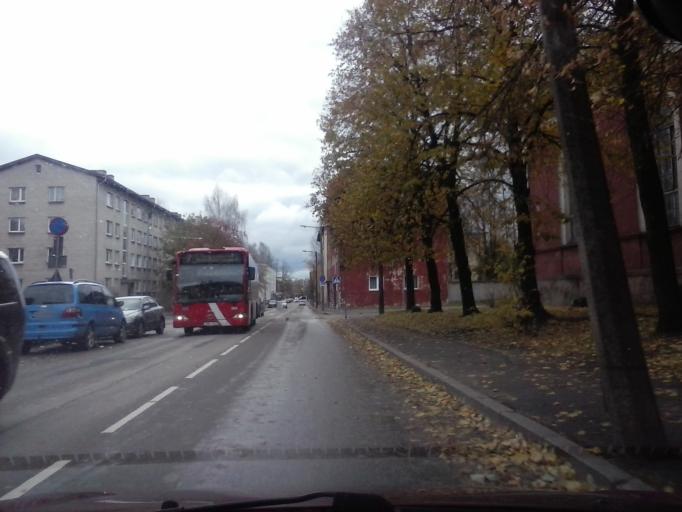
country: EE
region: Tartu
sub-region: Tartu linn
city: Tartu
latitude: 58.3767
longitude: 26.7171
